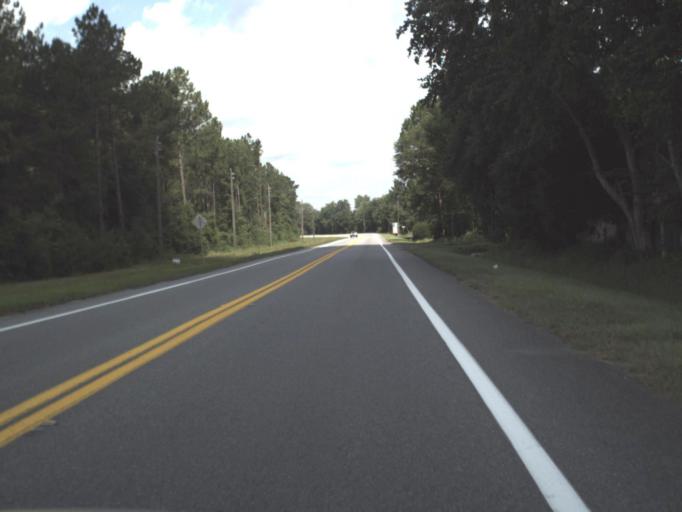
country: US
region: Florida
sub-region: Union County
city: Lake Butler
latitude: 30.0457
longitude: -82.2943
